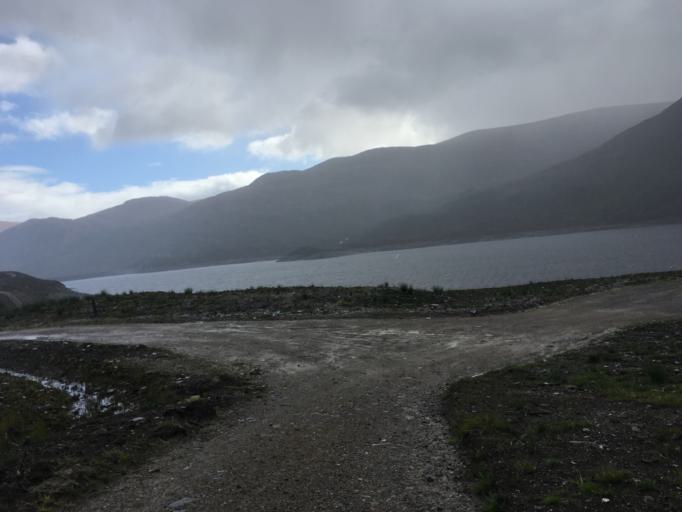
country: GB
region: Scotland
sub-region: Highland
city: Spean Bridge
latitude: 57.3418
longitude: -4.9815
